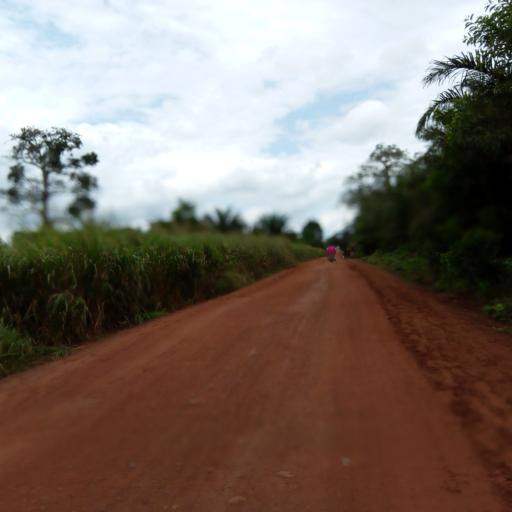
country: TG
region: Maritime
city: Tsevie
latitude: 6.3350
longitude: 1.0888
